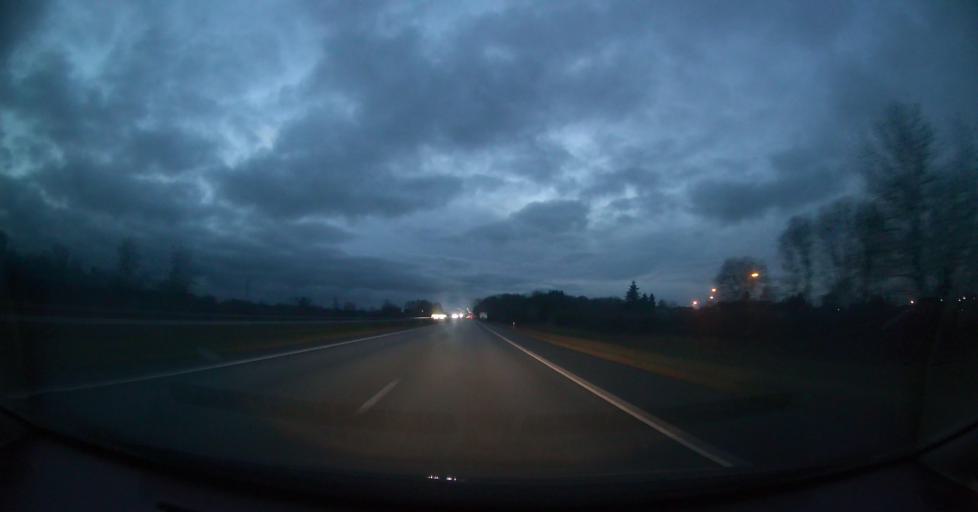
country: EE
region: Harju
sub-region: Kuusalu vald
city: Kuusalu
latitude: 59.4469
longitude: 25.3988
